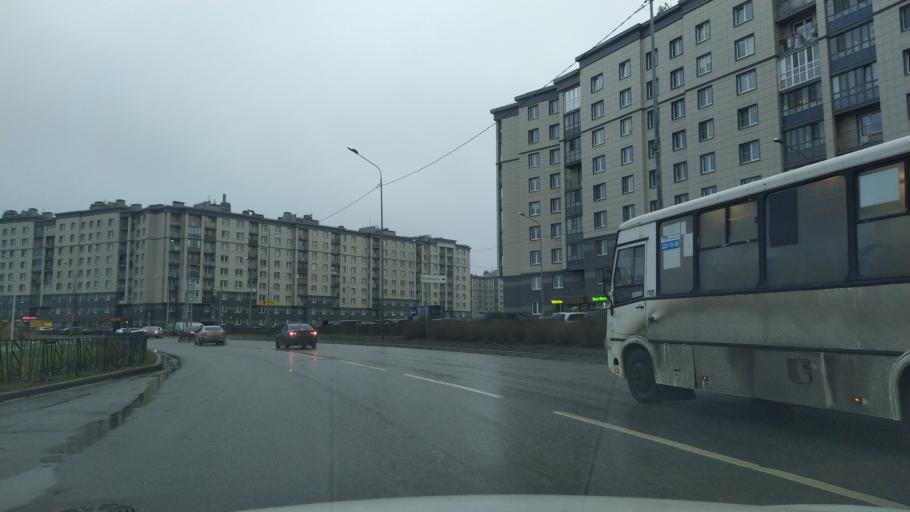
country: RU
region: St.-Petersburg
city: Tyarlevo
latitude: 59.7419
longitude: 30.4707
